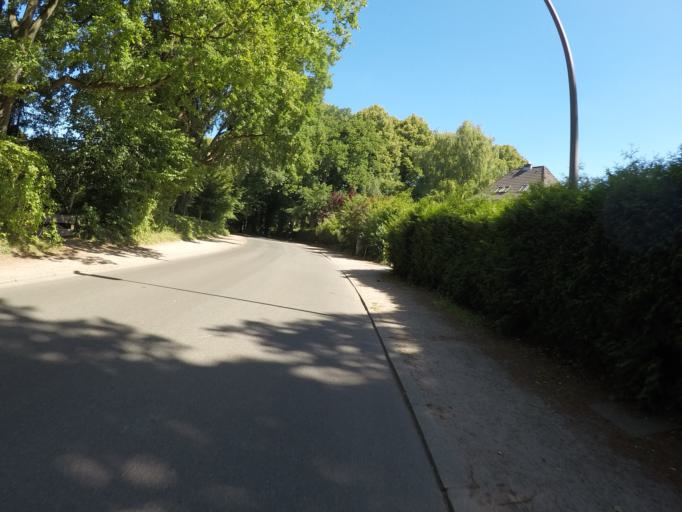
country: DE
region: Hamburg
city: Bergstedt
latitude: 53.6445
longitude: 10.1497
